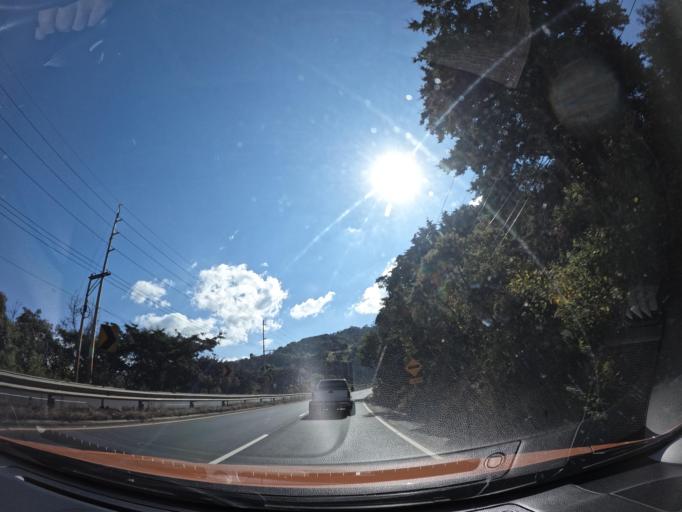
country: GT
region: Sacatepequez
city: Santiago Sacatepequez
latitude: 14.6216
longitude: -90.6842
